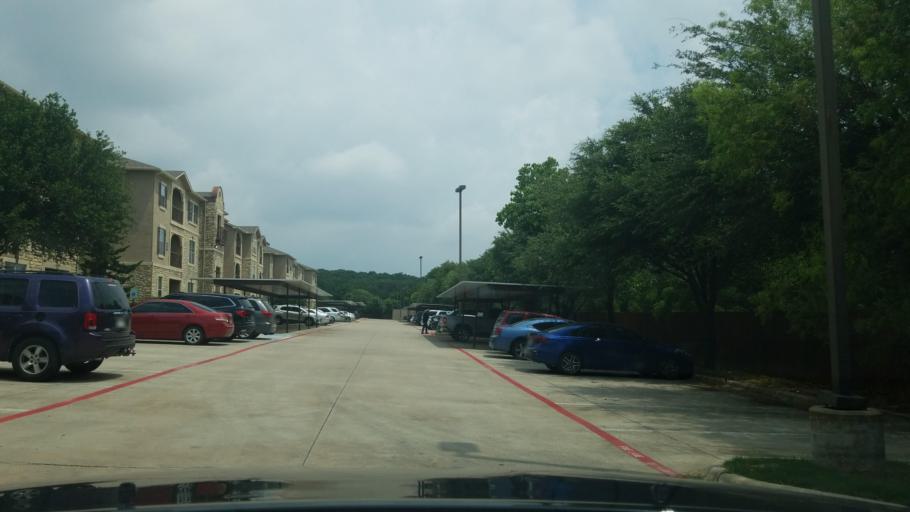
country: US
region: Texas
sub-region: Denton County
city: Corinth
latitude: 33.1850
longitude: -97.0916
